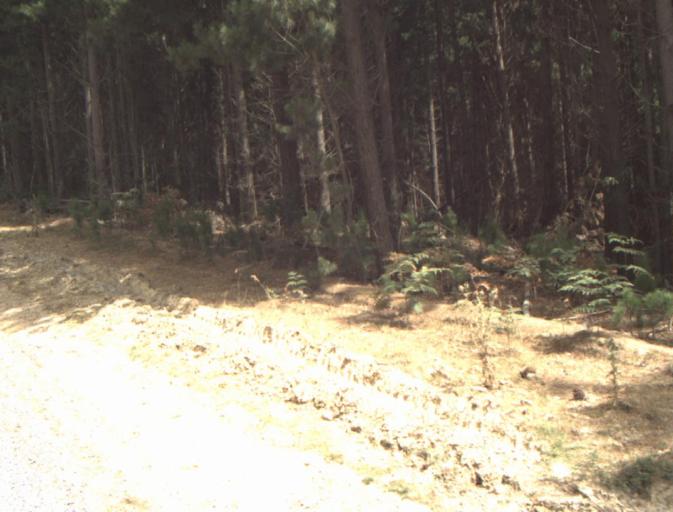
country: AU
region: Tasmania
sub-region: Launceston
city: Mayfield
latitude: -41.1718
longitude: 147.2002
